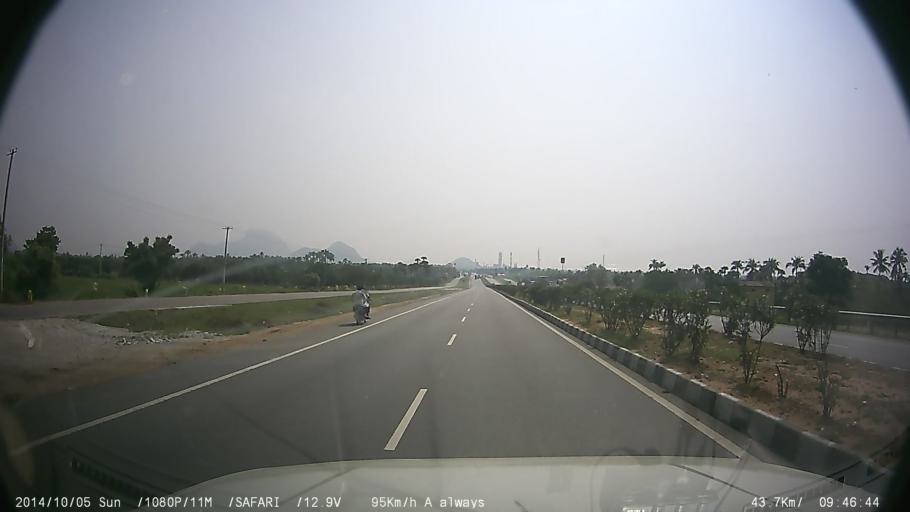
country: IN
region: Tamil Nadu
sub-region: Erode
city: Bhavani
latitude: 11.4549
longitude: 77.8016
